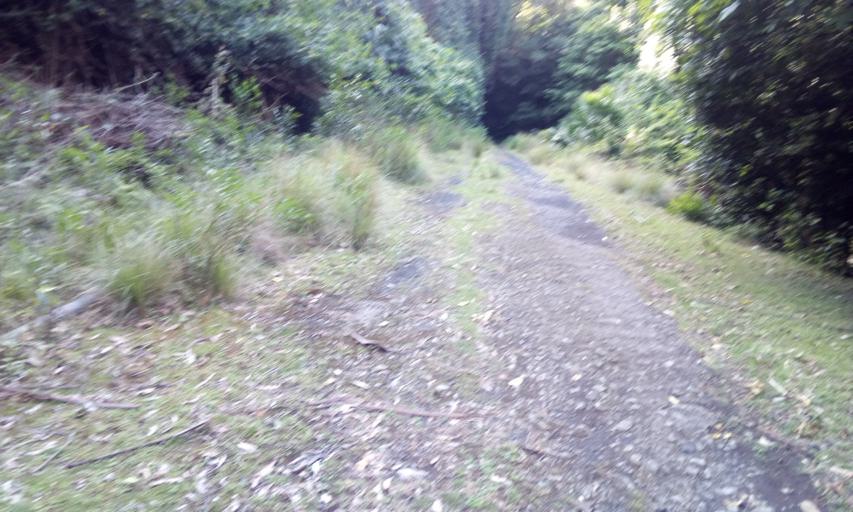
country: AU
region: New South Wales
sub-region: Wollongong
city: Cordeaux Heights
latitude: -34.4416
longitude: 150.8126
